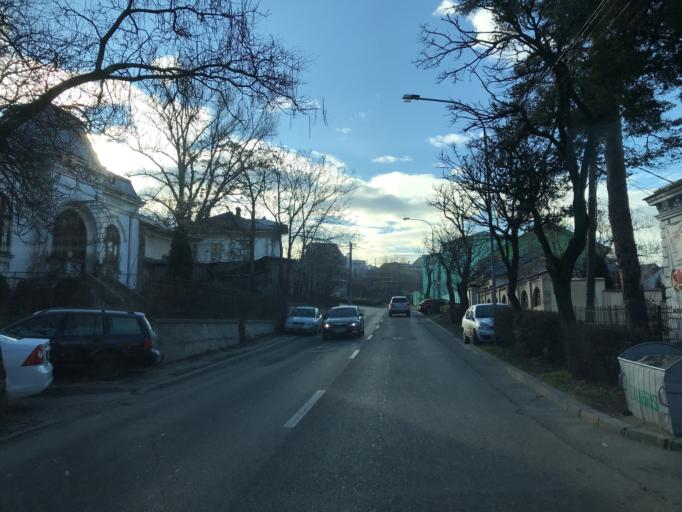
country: RO
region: Olt
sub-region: Municipiul Slatina
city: Slatina
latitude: 44.4293
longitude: 24.3611
